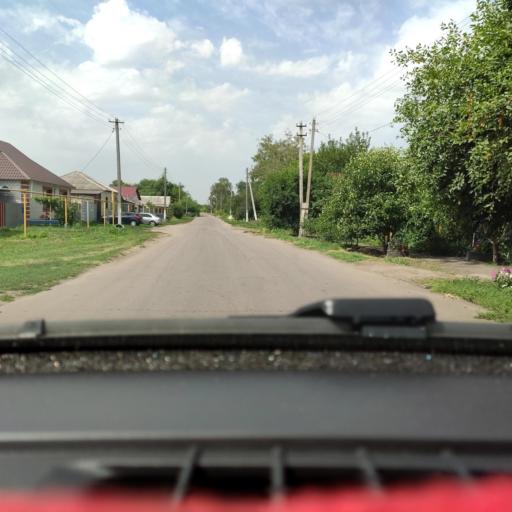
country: RU
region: Voronezj
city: Davydovka
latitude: 51.1956
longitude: 39.4916
